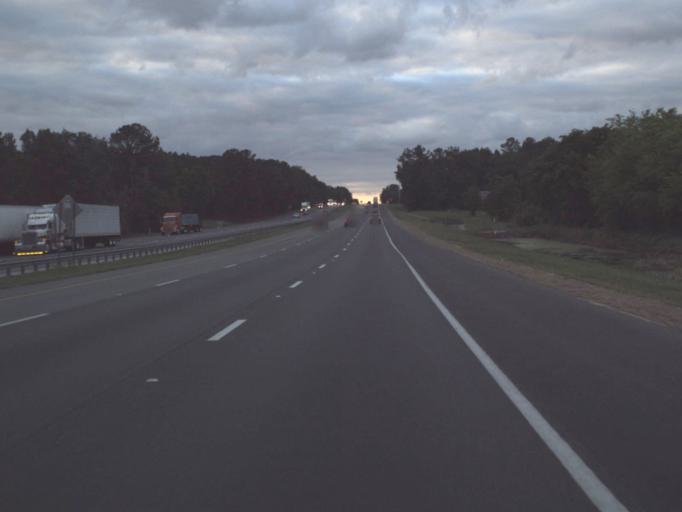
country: US
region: Florida
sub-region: Marion County
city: Citra
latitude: 29.3778
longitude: -82.2315
